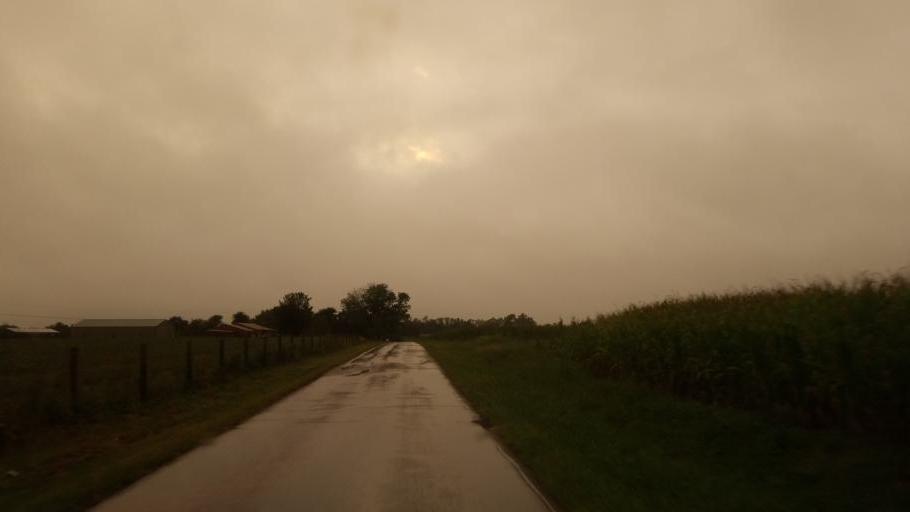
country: US
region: Kentucky
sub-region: Fleming County
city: Flemingsburg
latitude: 38.4681
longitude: -83.6332
